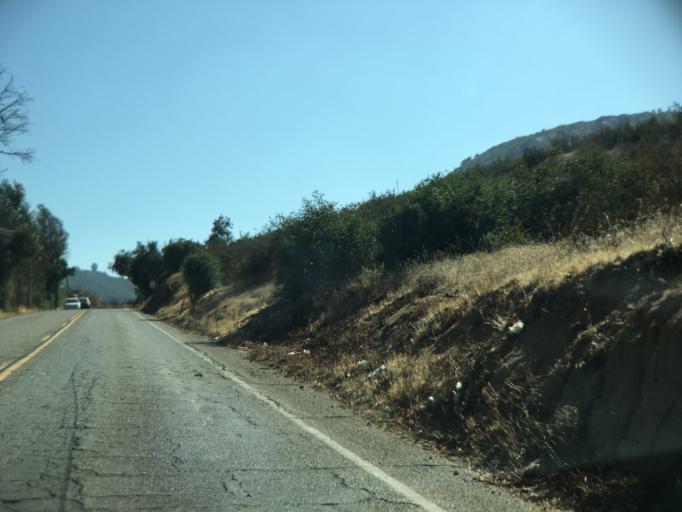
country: US
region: California
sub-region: San Diego County
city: Valley Center
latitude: 33.2423
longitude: -116.9643
